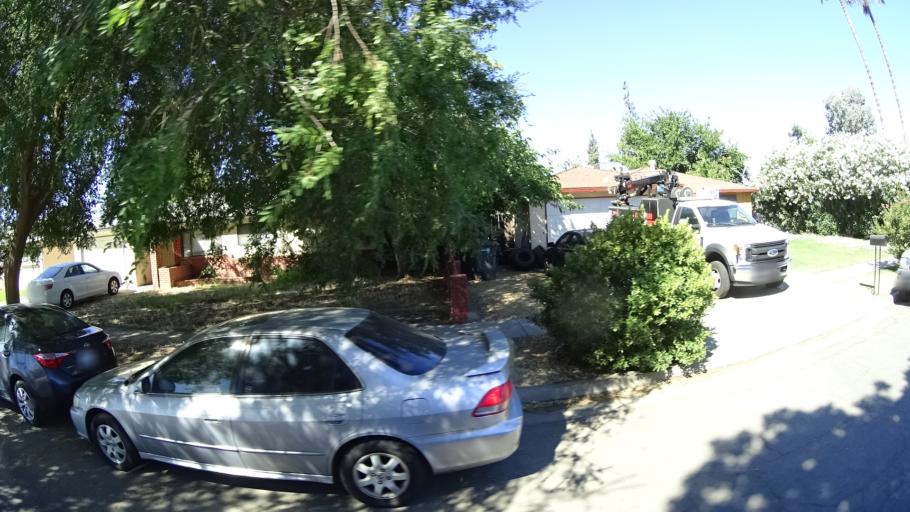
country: US
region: California
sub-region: Fresno County
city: Fresno
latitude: 36.8005
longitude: -119.8432
